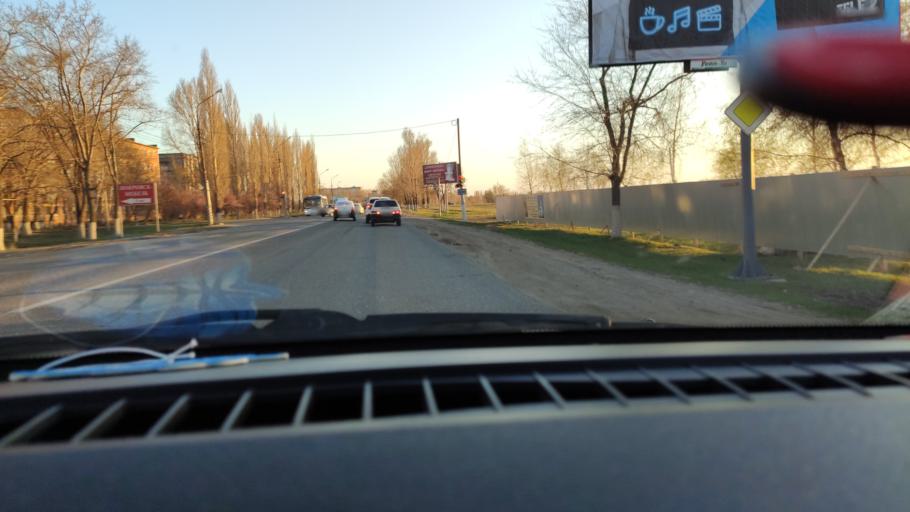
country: RU
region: Saratov
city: Engel's
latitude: 51.4528
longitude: 46.0841
